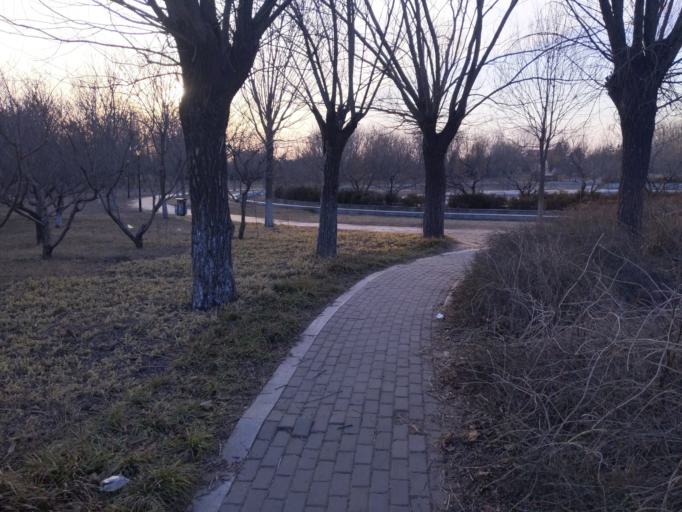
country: CN
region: Henan Sheng
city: Puyang
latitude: 35.7821
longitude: 114.9487
